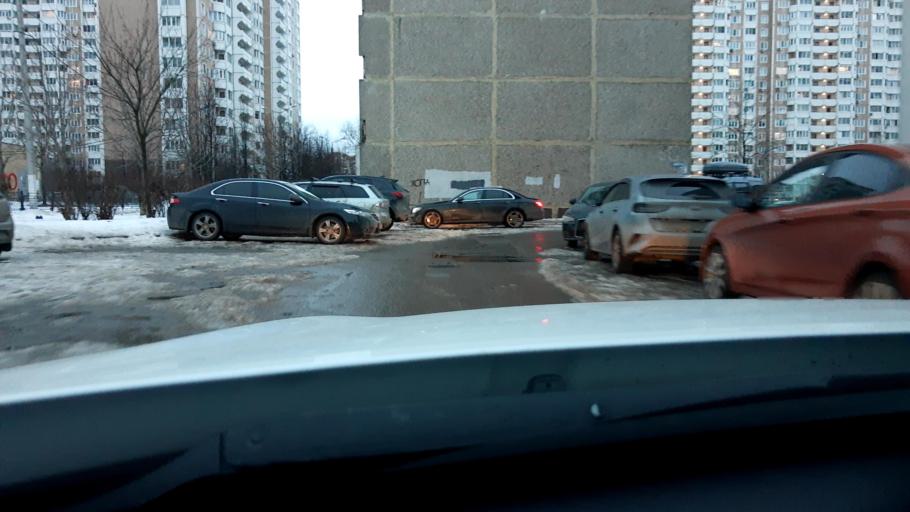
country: RU
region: Moskovskaya
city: Domodedovo
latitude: 55.4539
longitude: 37.7458
